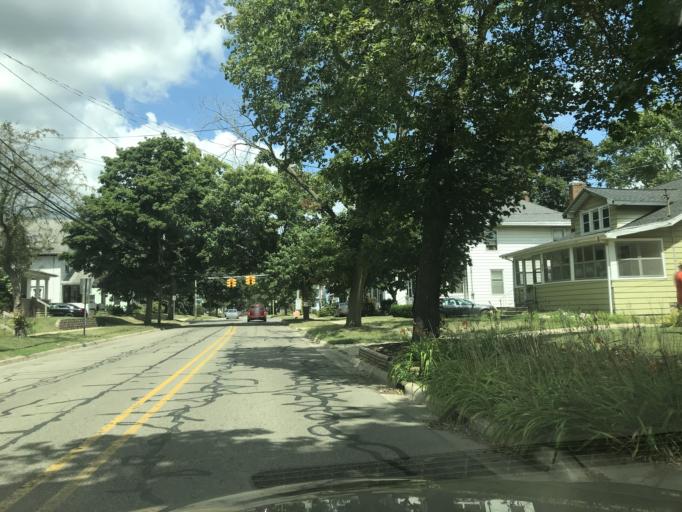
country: US
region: Michigan
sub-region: Jackson County
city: Jackson
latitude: 42.2394
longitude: -84.4185
